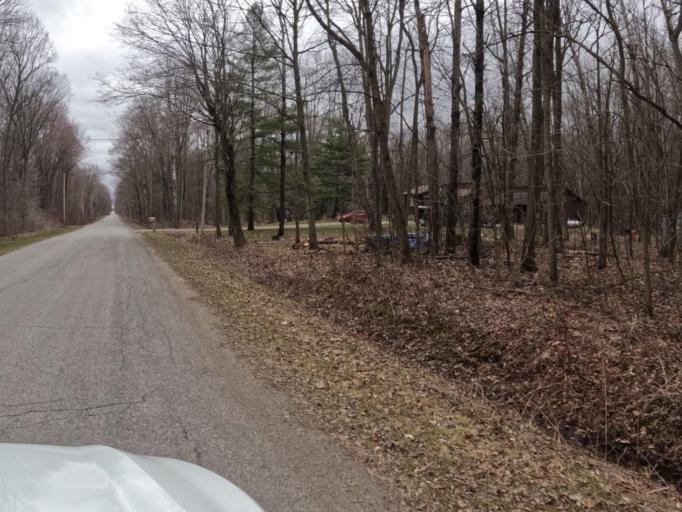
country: CA
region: Ontario
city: Norfolk County
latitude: 42.9789
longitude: -80.4166
